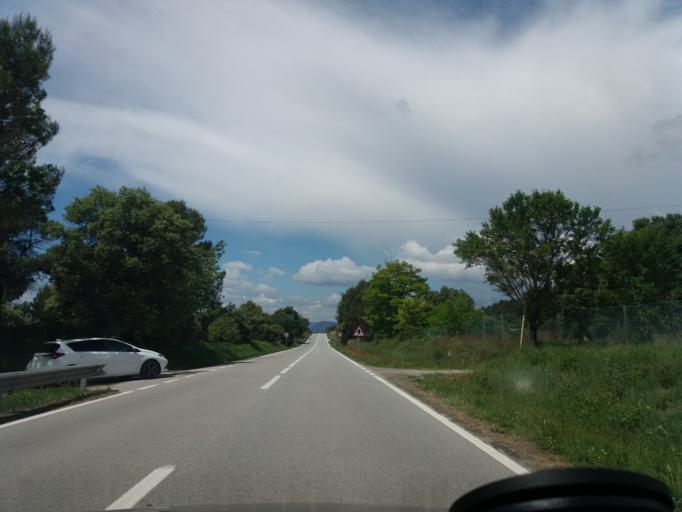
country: ES
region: Catalonia
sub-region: Provincia de Barcelona
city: Navarcles
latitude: 41.7663
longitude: 1.9241
